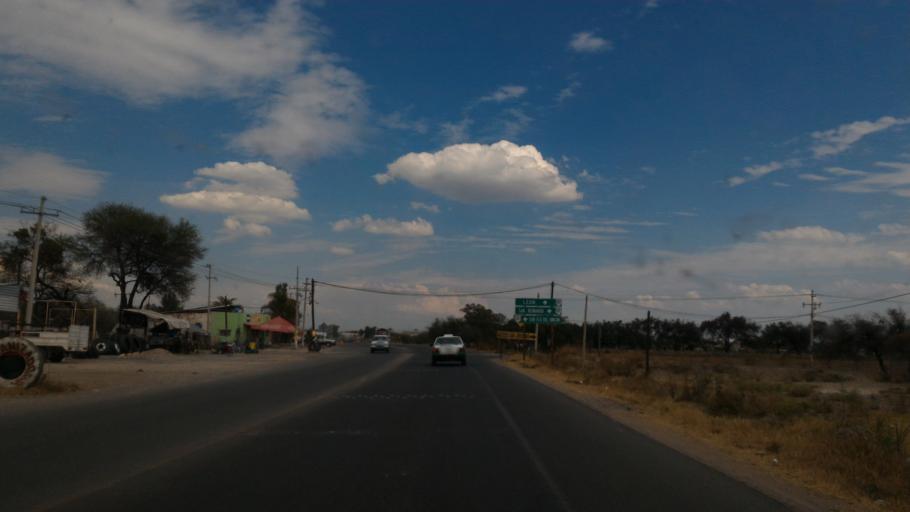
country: MX
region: Guanajuato
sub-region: Purisima del Rincon
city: Monte Grande
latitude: 20.9979
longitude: -101.8586
